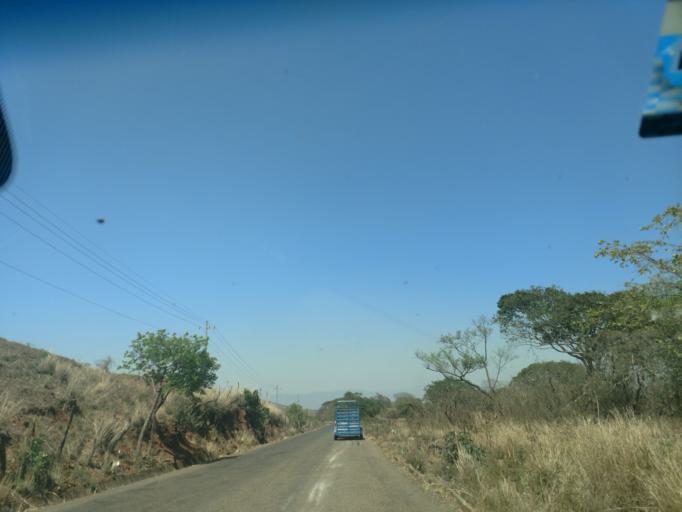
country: MX
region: Nayarit
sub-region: Tepic
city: La Corregidora
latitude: 21.5019
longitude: -104.7348
